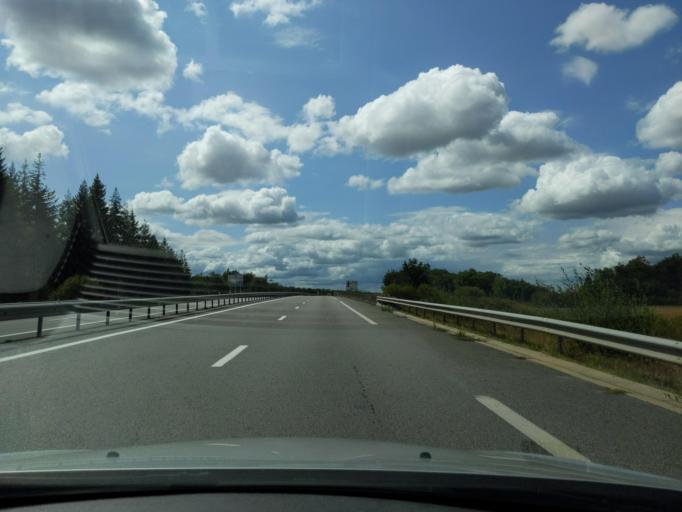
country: FR
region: Limousin
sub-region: Departement de la Creuse
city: Gouzon
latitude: 46.1958
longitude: 2.1804
